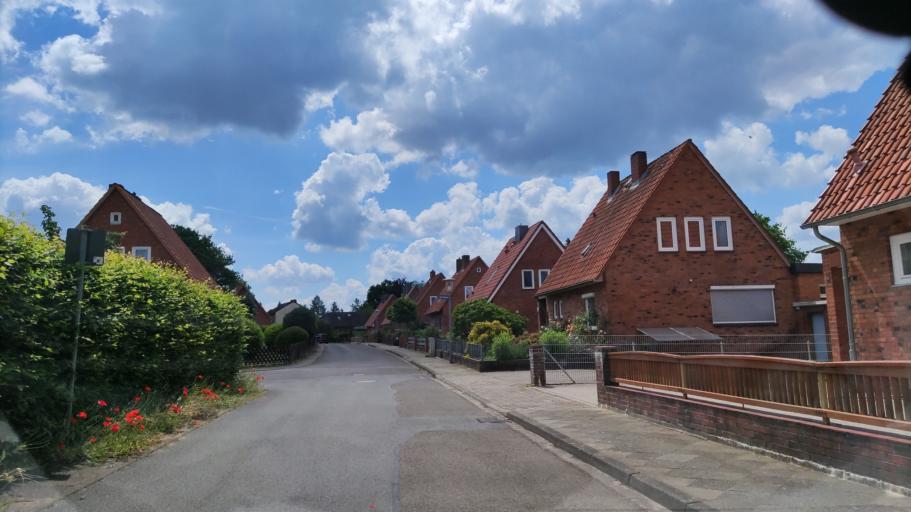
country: DE
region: Lower Saxony
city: Deutsch Evern
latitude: 53.2053
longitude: 10.4399
